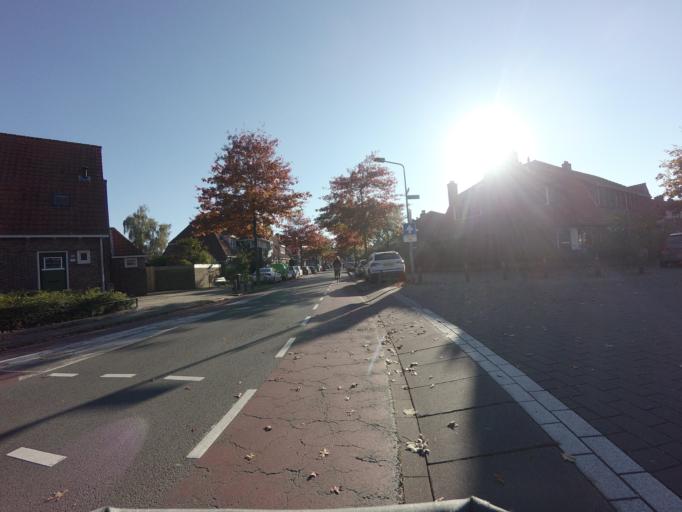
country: NL
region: North Holland
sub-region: Gemeente Hilversum
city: Hilversum
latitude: 52.2134
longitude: 5.1679
